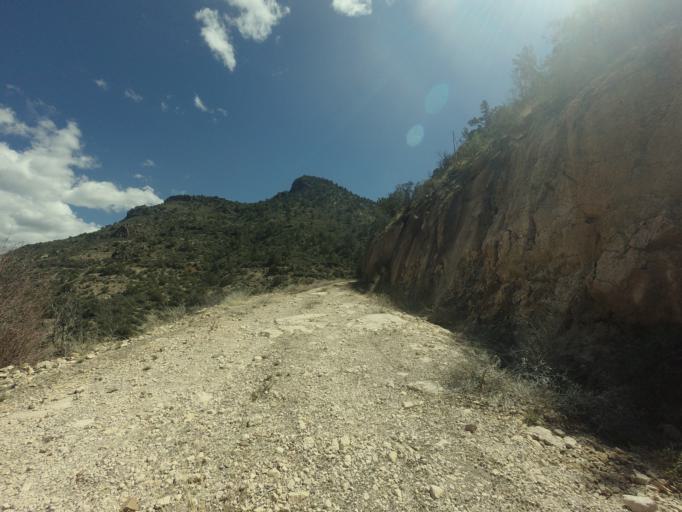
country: US
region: Arizona
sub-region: Gila County
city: Pine
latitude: 34.4028
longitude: -111.5991
